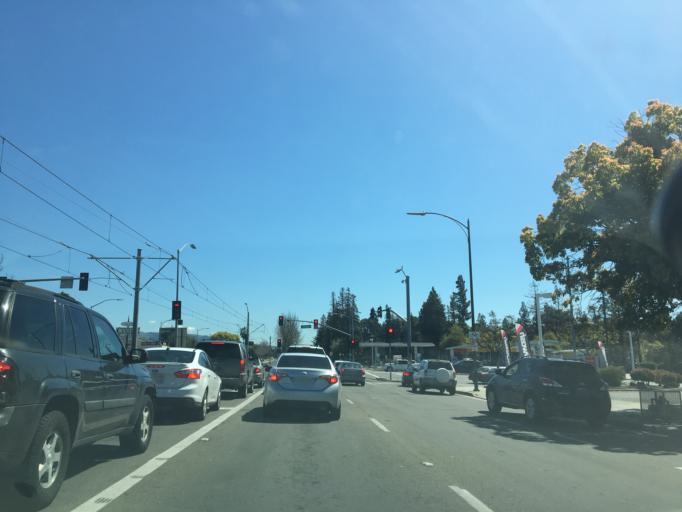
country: US
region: California
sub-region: Santa Clara County
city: Alum Rock
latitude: 37.3706
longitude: -121.8437
